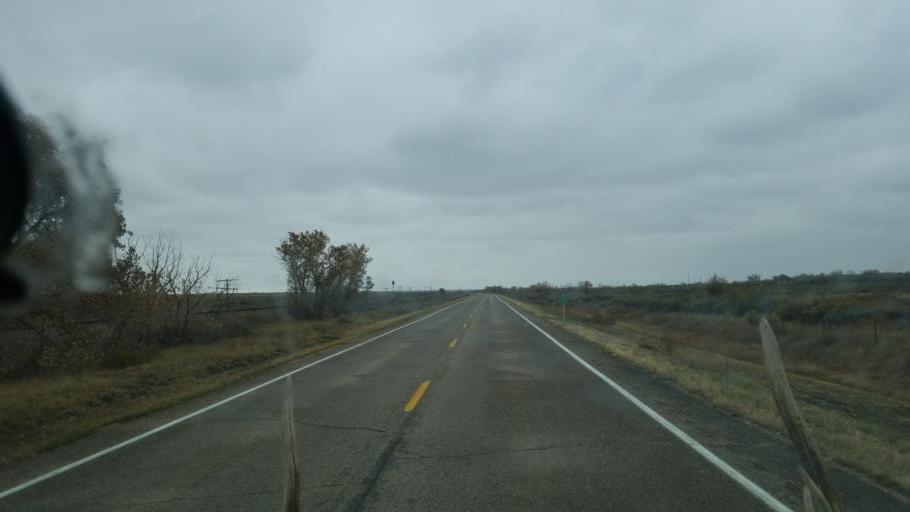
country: US
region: Colorado
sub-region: Pueblo County
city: Pueblo
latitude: 38.2547
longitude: -104.3057
